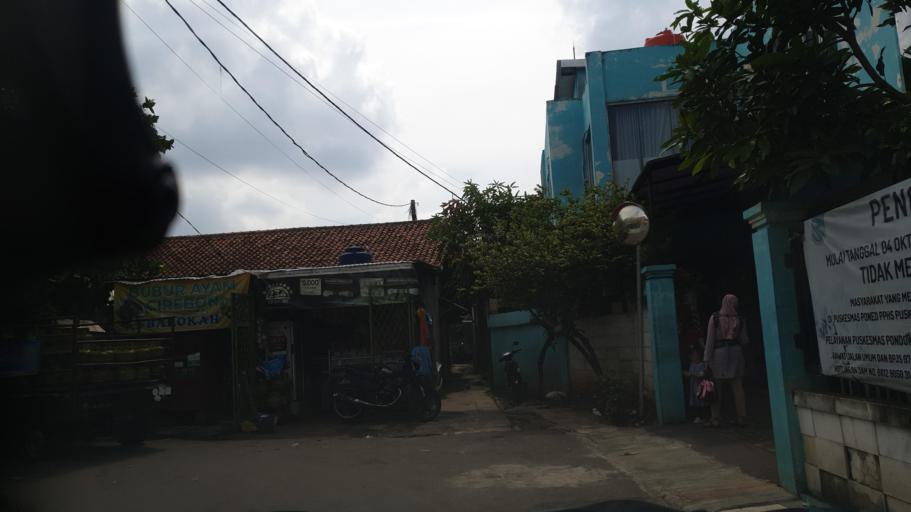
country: ID
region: West Java
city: Pamulang
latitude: -6.3399
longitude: 106.7694
